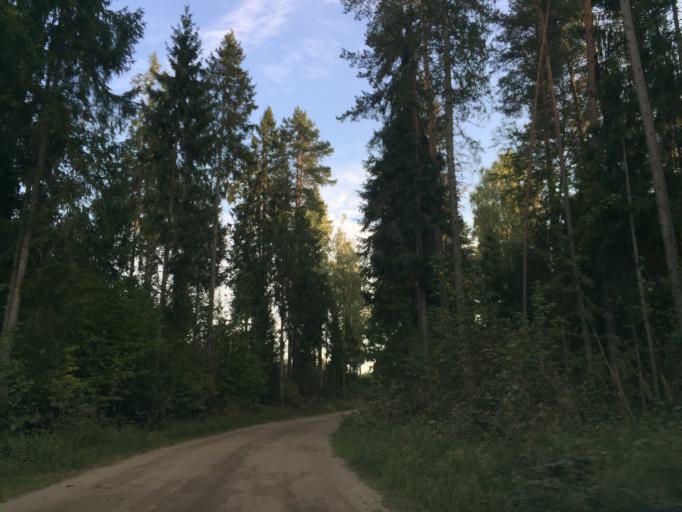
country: LV
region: Baldone
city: Baldone
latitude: 56.7658
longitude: 24.4070
